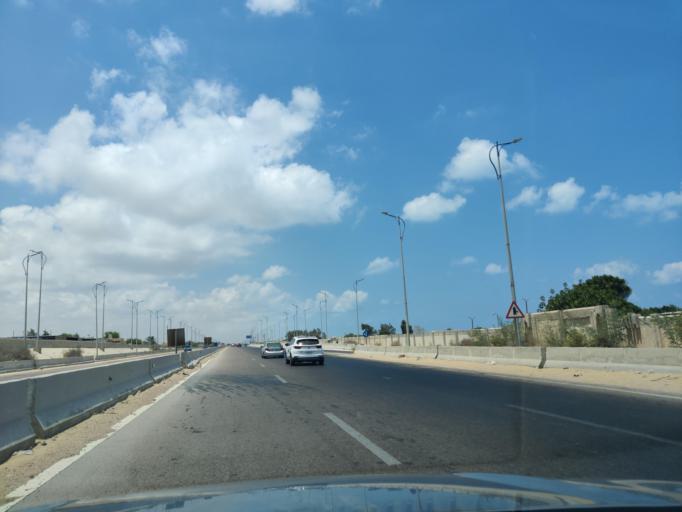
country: EG
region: Alexandria
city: Alexandria
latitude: 30.9456
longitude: 29.5112
